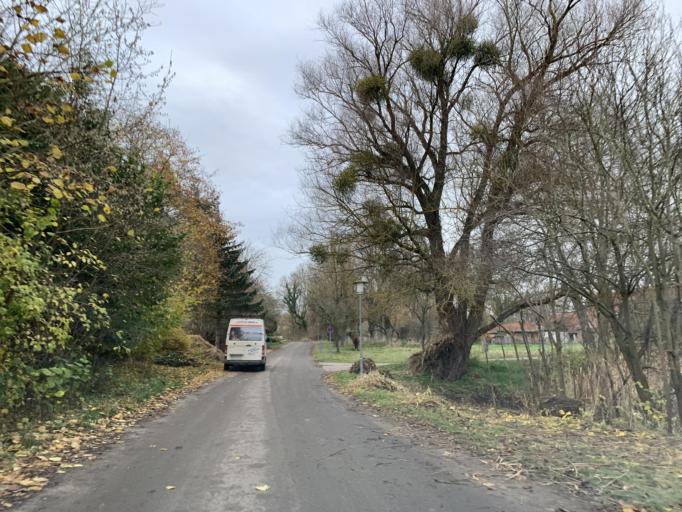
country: DE
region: Mecklenburg-Vorpommern
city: Carpin
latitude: 53.4045
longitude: 13.2001
